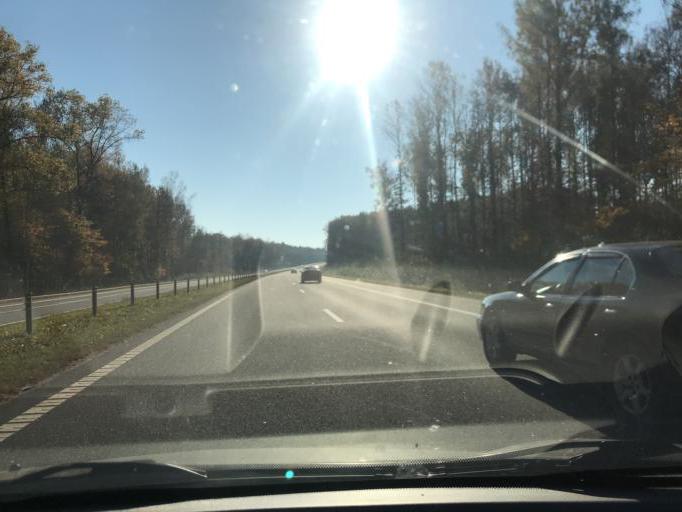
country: BY
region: Minsk
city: Pukhavichy
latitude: 53.4421
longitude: 28.4261
